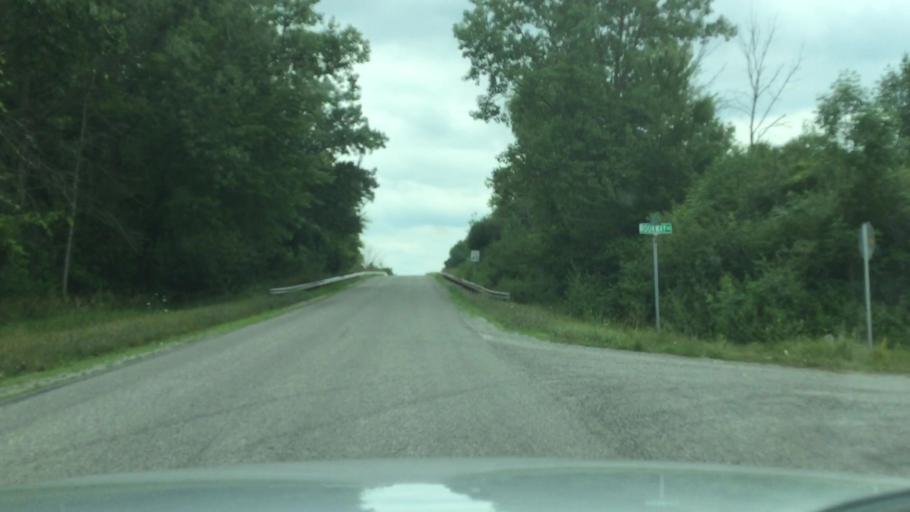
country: US
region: Michigan
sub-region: Saginaw County
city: Bridgeport
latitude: 43.3217
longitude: -83.8521
